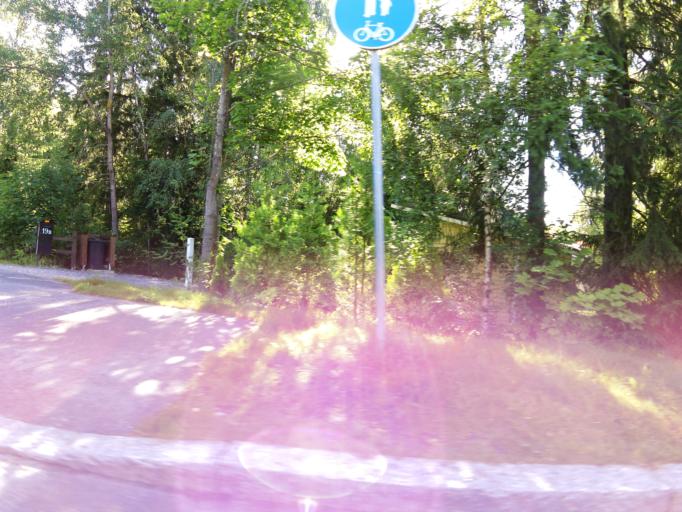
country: FI
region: Uusimaa
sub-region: Helsinki
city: Espoo
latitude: 60.1602
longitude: 24.6673
